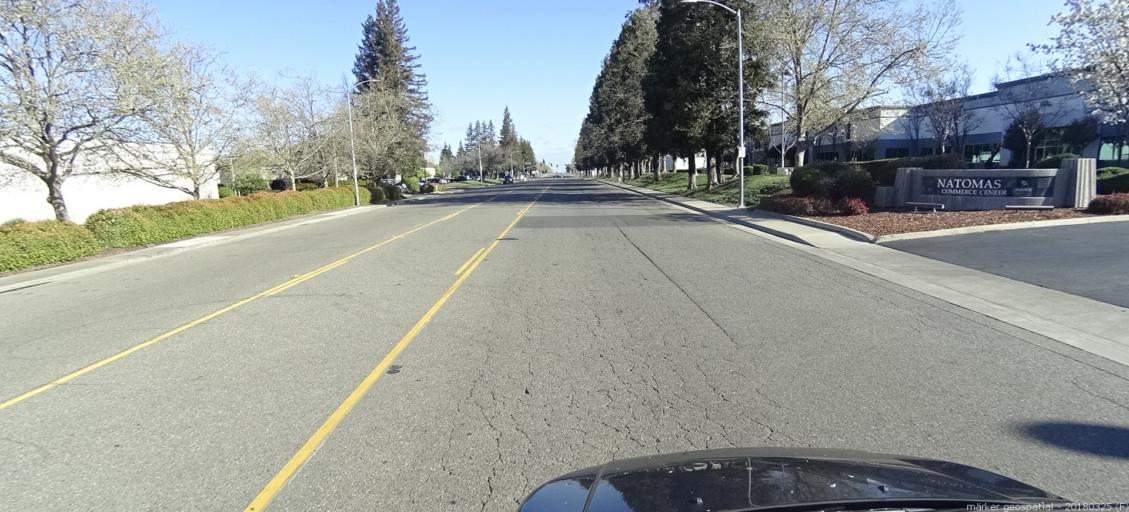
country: US
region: California
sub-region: Sacramento County
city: Rio Linda
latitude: 38.6444
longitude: -121.4876
